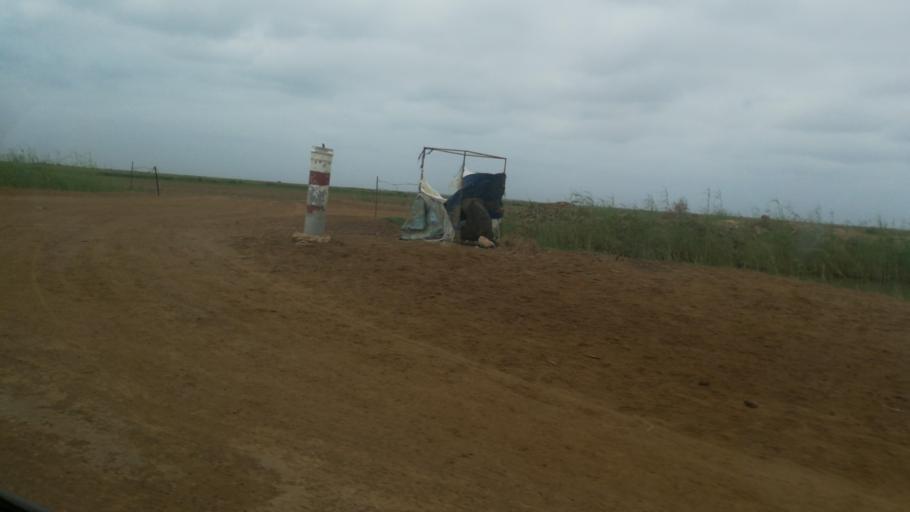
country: SN
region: Saint-Louis
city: Saint-Louis
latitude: 16.3163
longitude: -16.2328
